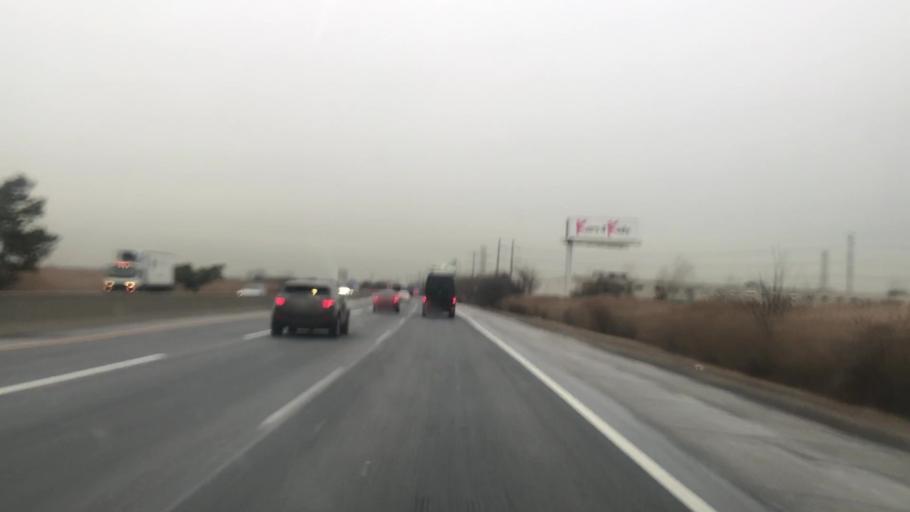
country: US
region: New Jersey
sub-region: Hudson County
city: North Bergen
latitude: 40.8060
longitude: -74.0322
